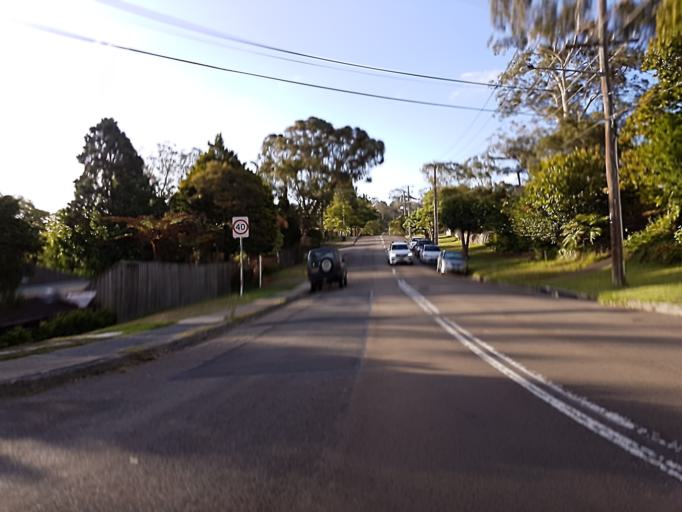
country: AU
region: New South Wales
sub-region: Warringah
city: Davidson
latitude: -33.7474
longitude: 151.2185
